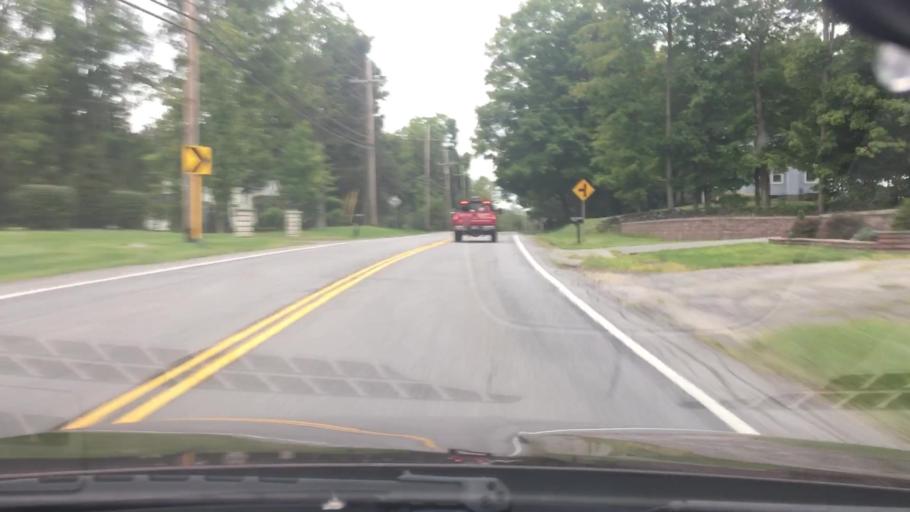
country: US
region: New York
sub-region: Dutchess County
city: Pleasant Valley
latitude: 41.7551
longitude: -73.7896
